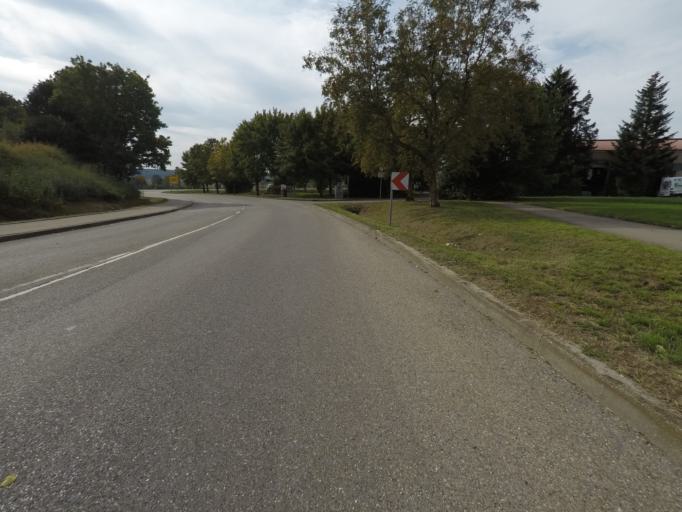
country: DE
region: Baden-Wuerttemberg
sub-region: Regierungsbezirk Stuttgart
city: Ehningen
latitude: 48.6524
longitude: 8.9295
